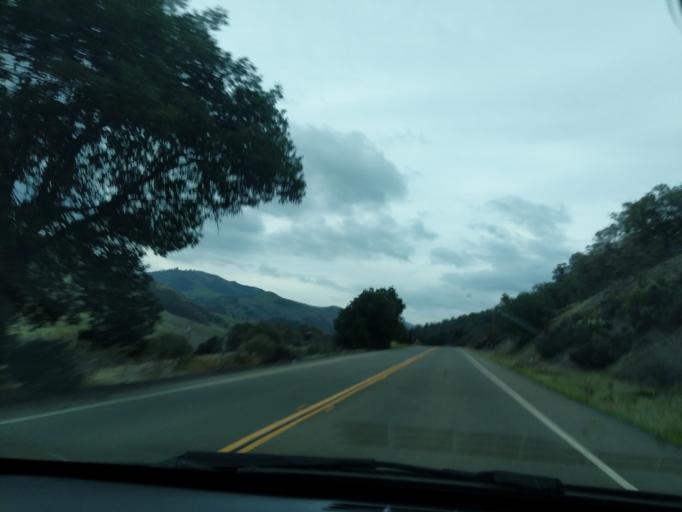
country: US
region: California
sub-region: Monterey County
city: Soledad
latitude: 36.6106
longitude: -121.2052
